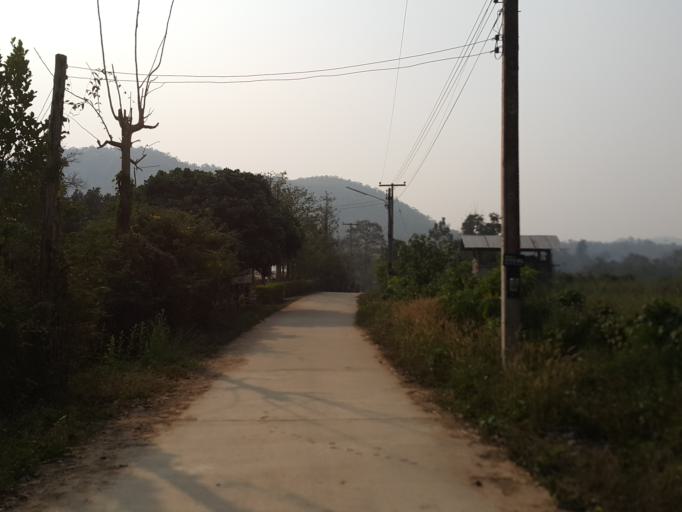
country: TH
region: Lamphun
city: Li
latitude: 17.6051
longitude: 98.9680
